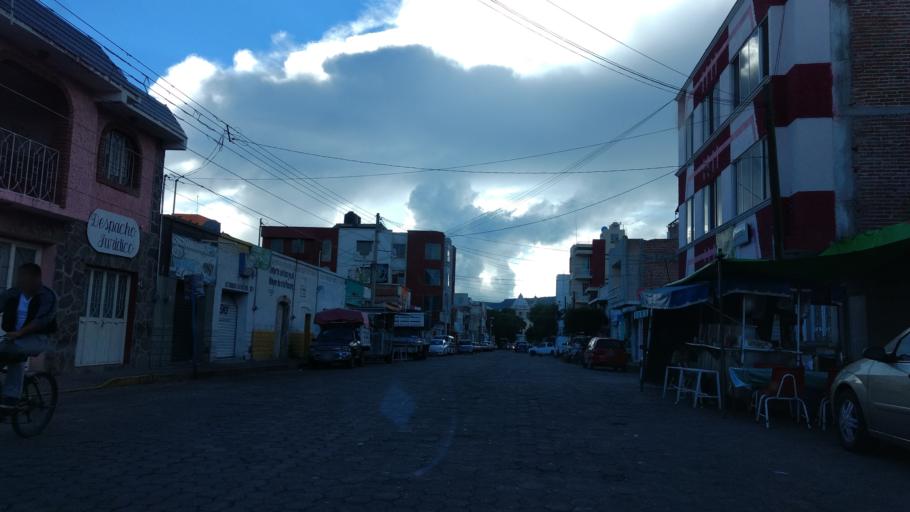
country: MX
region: Zacatecas
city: Tlaltenango de Sanchez Roman
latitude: 21.7813
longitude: -103.3019
